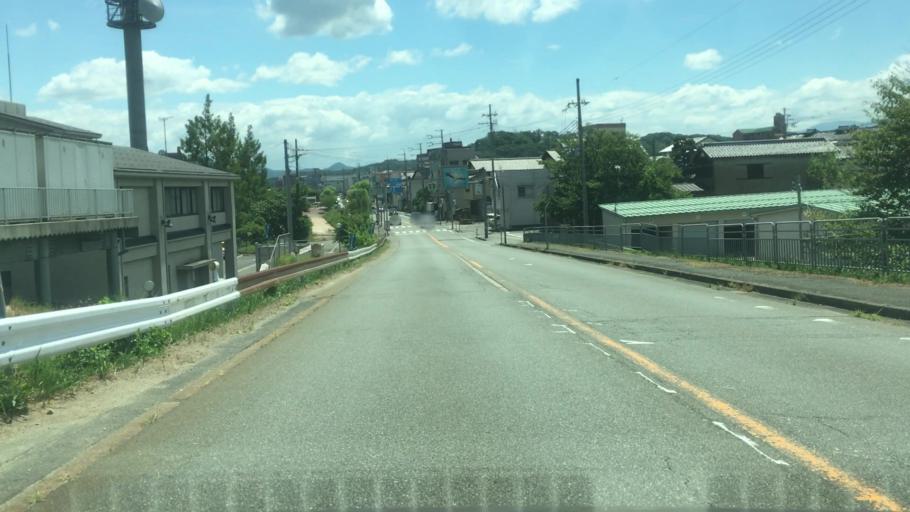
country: JP
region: Hyogo
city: Toyooka
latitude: 35.5471
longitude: 134.8261
